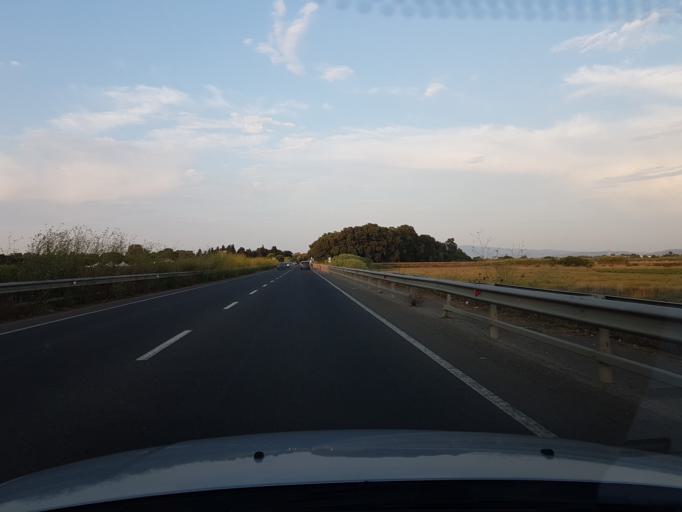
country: IT
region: Sardinia
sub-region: Provincia di Oristano
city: Solanas
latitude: 39.9195
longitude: 8.5603
